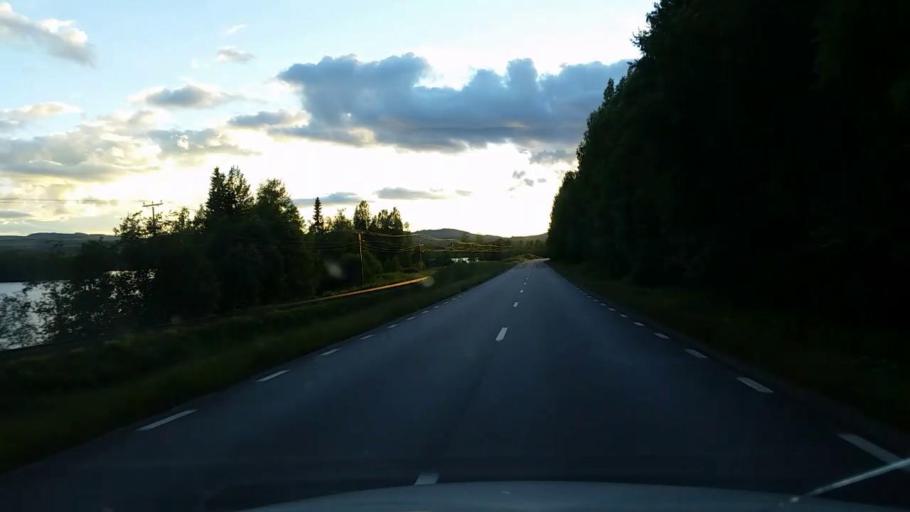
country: SE
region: Gaevleborg
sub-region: Ljusdals Kommun
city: Farila
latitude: 62.1294
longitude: 15.7046
